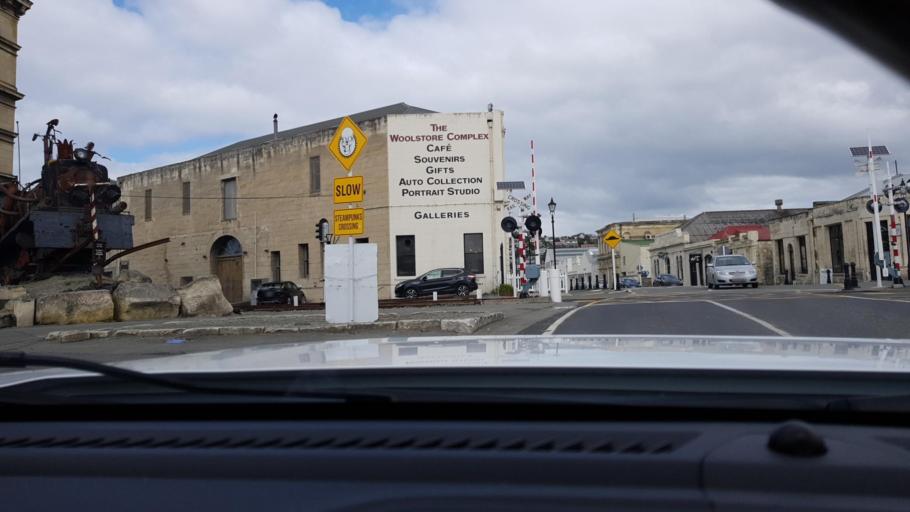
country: NZ
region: Otago
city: Oamaru
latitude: -45.1021
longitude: 170.9704
